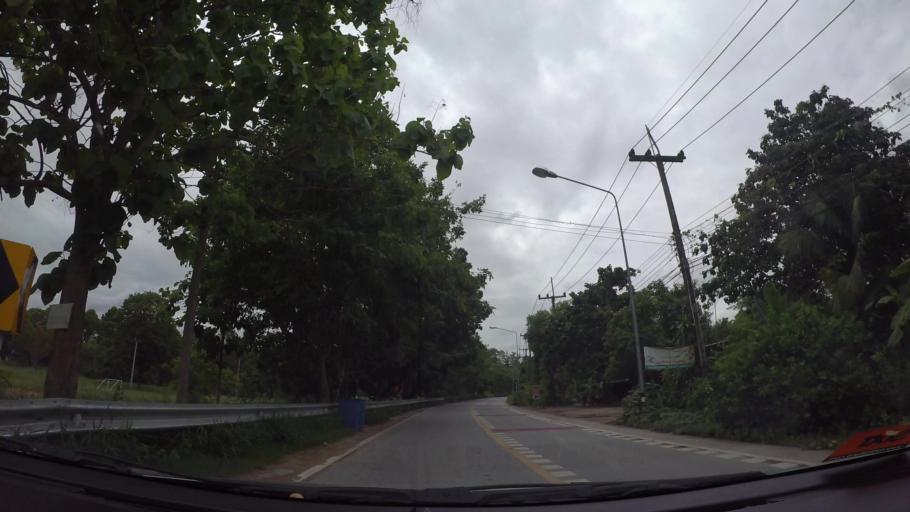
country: TH
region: Chon Buri
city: Si Racha
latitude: 13.1872
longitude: 100.9779
